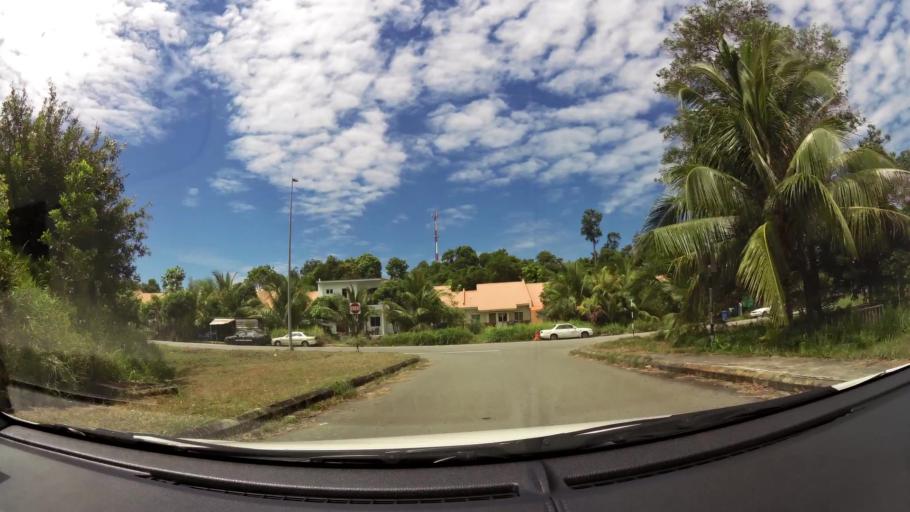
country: BN
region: Brunei and Muara
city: Bandar Seri Begawan
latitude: 4.9921
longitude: 115.0079
